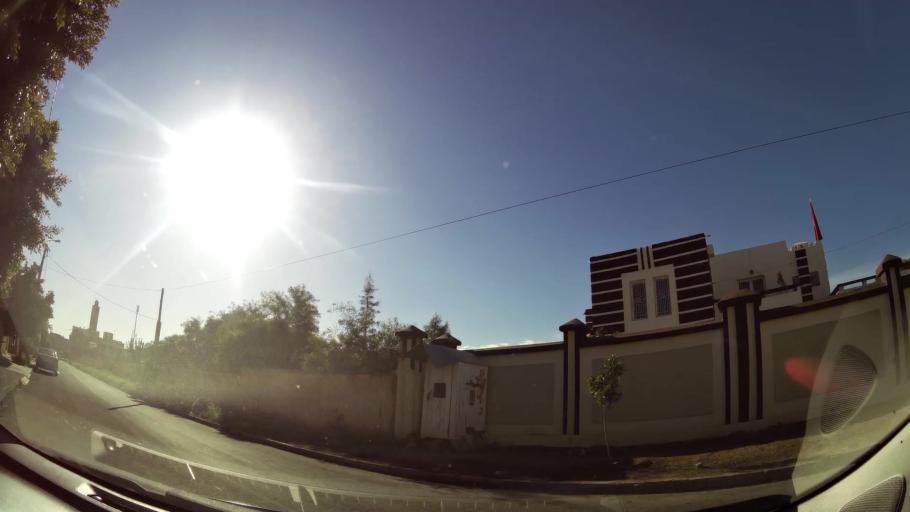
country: MA
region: Oriental
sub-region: Oujda-Angad
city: Oujda
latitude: 34.6589
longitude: -1.9091
